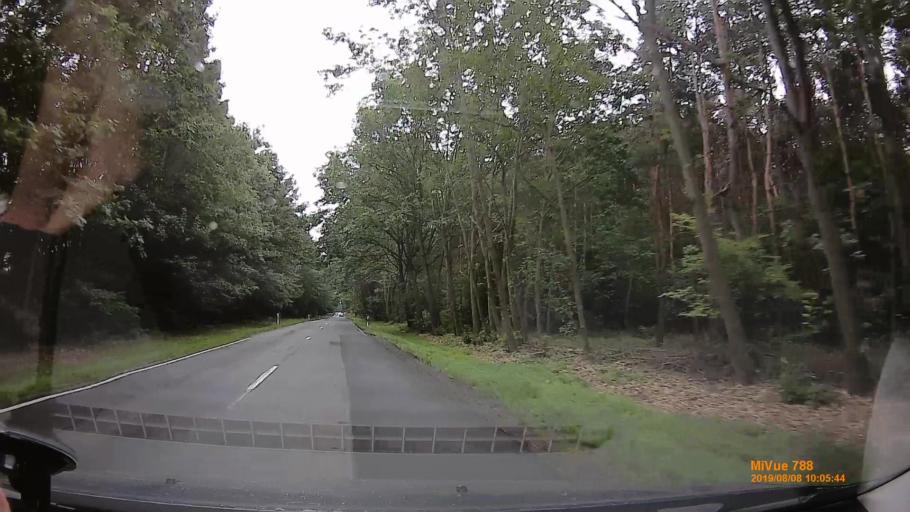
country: HU
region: Zala
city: Zalaegerszeg
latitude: 46.8975
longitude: 16.8568
